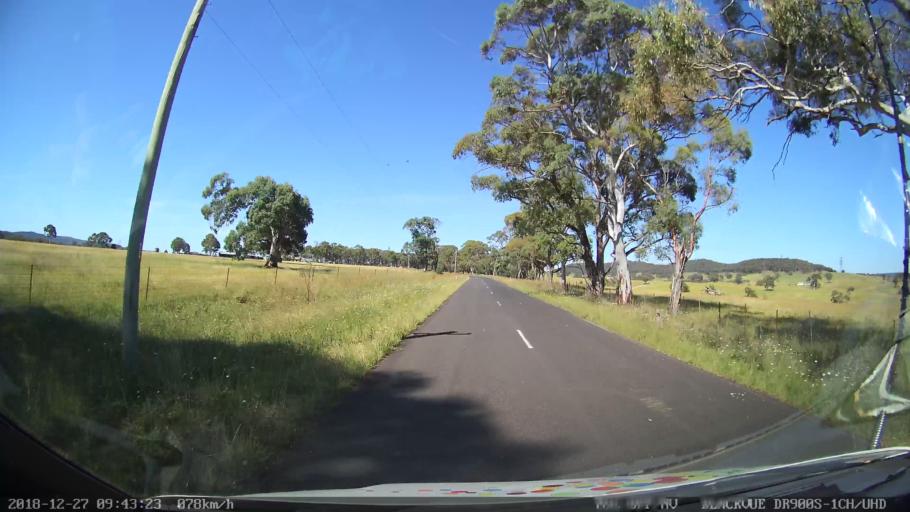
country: AU
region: New South Wales
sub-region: Lithgow
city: Portland
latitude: -33.3058
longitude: 150.0016
